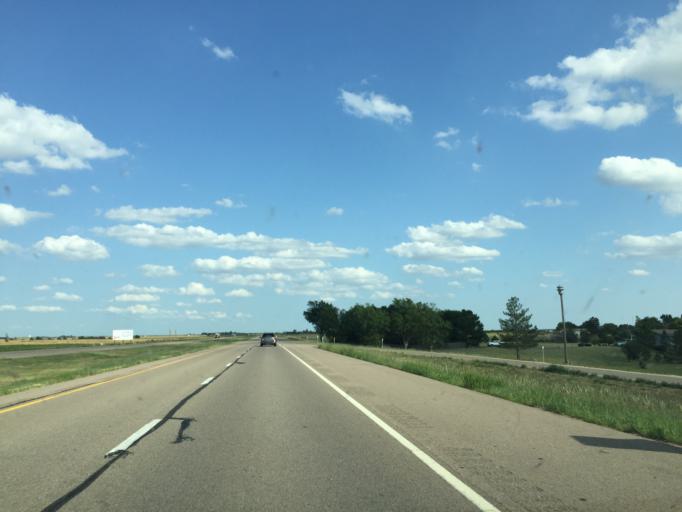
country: US
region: Kansas
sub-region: Gove County
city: Gove
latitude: 39.0571
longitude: -100.2402
